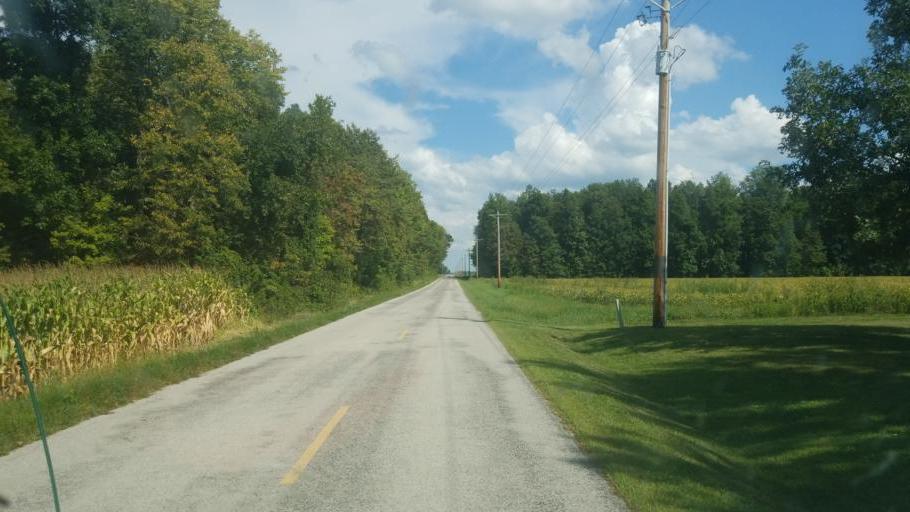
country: US
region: Ohio
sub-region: Seneca County
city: Tiffin
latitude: 40.9935
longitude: -83.1036
